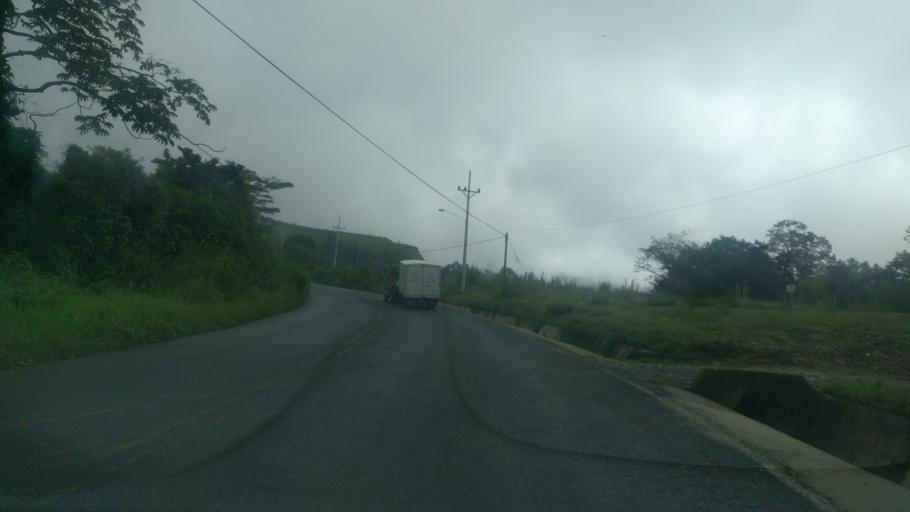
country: CR
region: Alajuela
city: San Rafael
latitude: 10.0354
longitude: -84.5118
